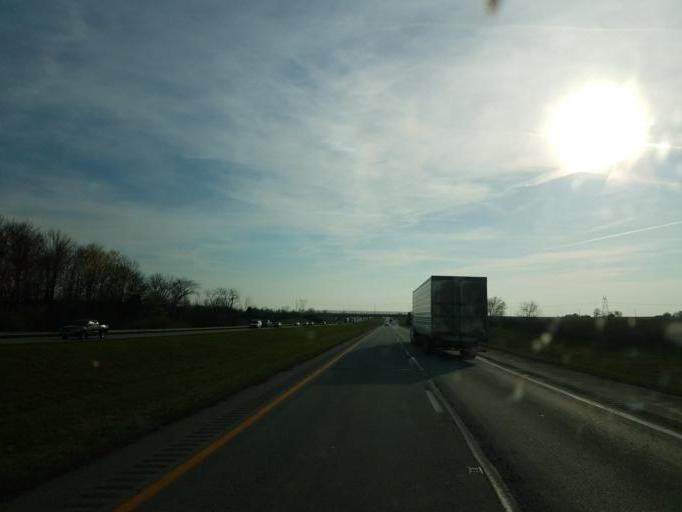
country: US
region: Ohio
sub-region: Clinton County
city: Wilmington
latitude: 39.5129
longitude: -83.8639
